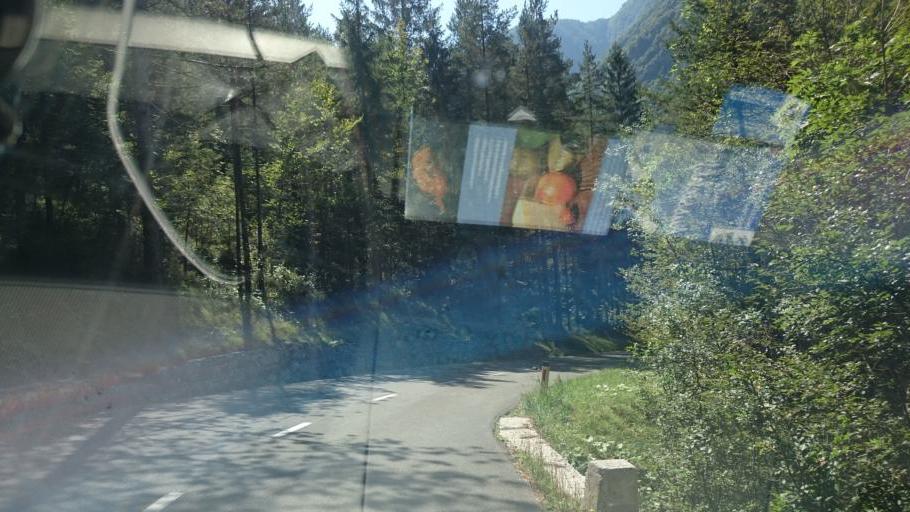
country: SI
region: Bovec
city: Bovec
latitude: 46.3781
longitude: 13.5859
